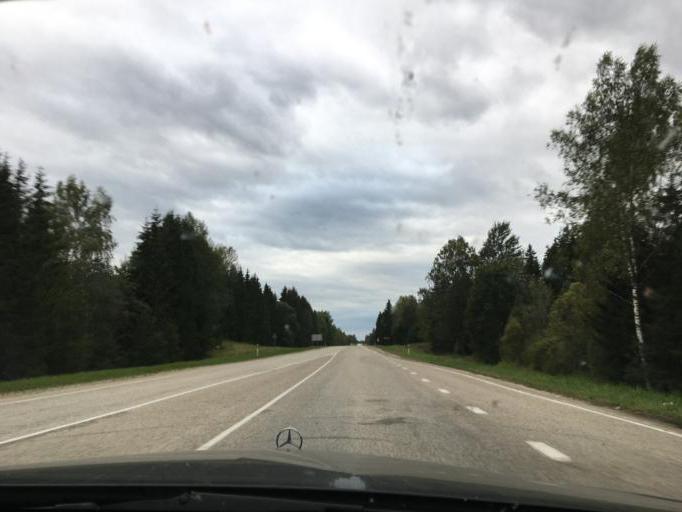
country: RU
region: Pskov
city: Pechory
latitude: 57.6356
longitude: 27.3390
